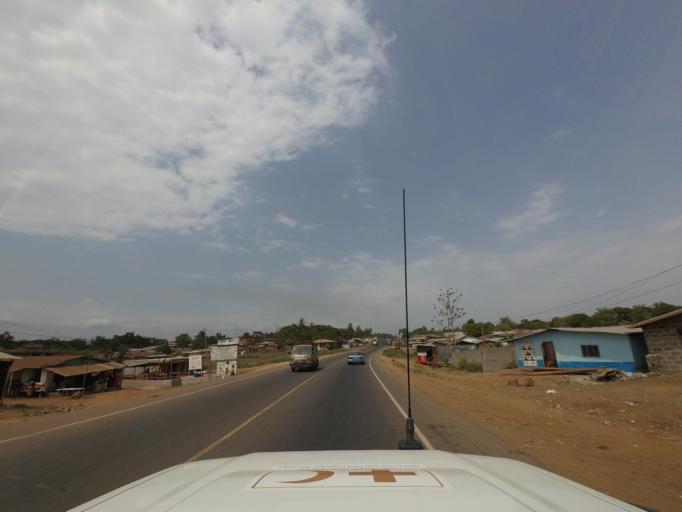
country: LR
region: Montserrado
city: Bensonville City
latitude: 6.3481
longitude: -10.6550
